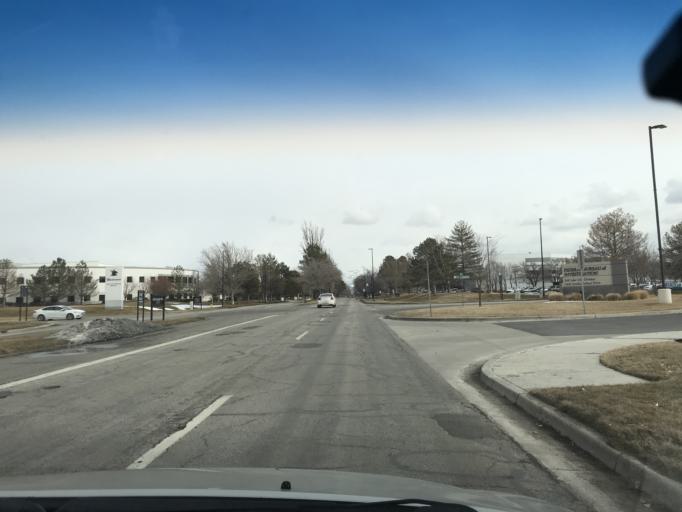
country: US
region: Utah
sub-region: Salt Lake County
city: West Valley City
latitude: 40.7763
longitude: -112.0204
